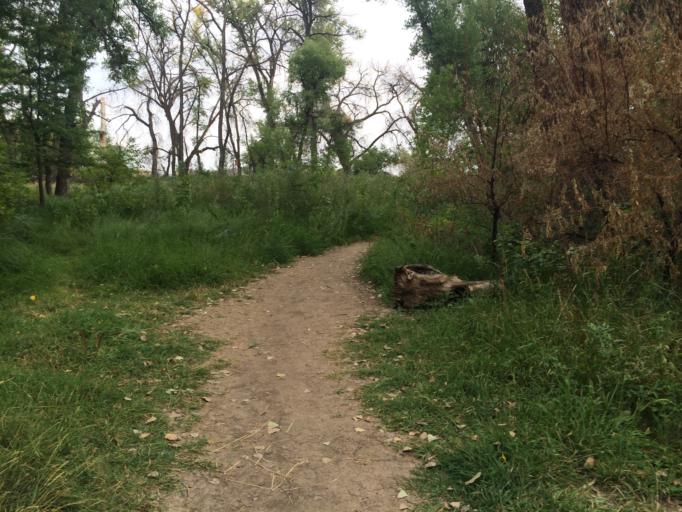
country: US
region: Colorado
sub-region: Adams County
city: Northglenn
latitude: 39.9568
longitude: -105.0109
